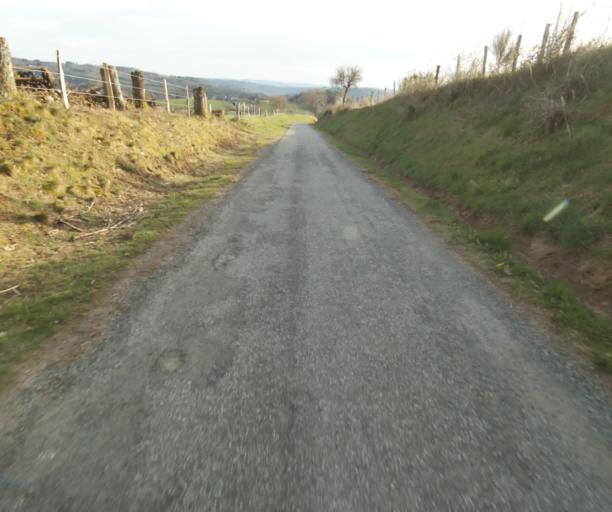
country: FR
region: Limousin
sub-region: Departement de la Correze
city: Correze
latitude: 45.3718
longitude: 1.8341
